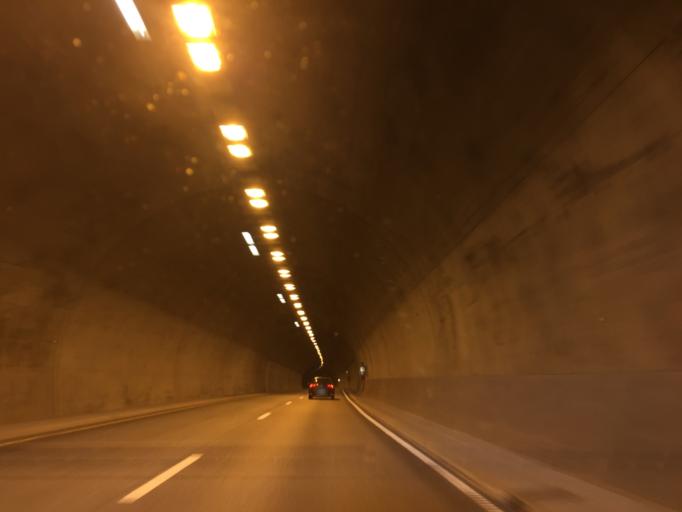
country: NO
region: Akershus
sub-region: Skedsmo
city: Lillestrom
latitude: 59.9401
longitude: 11.0152
